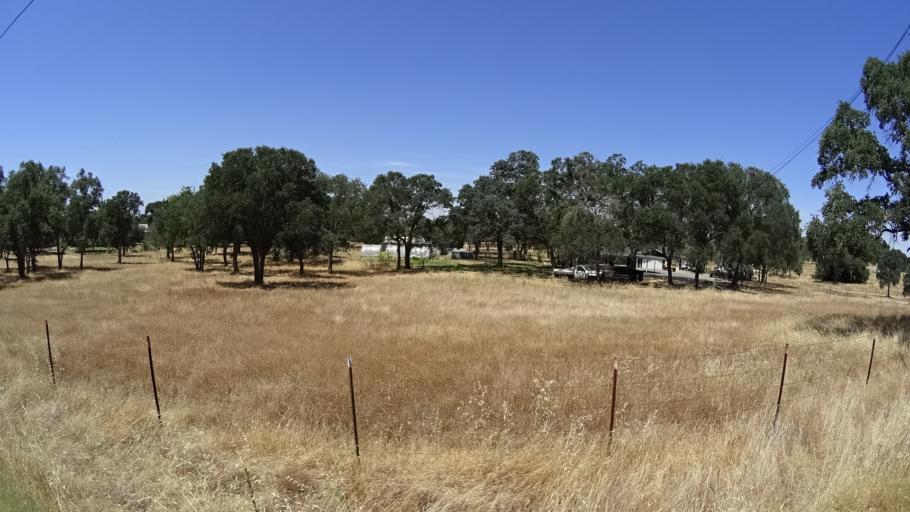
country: US
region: California
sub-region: Calaveras County
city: Rancho Calaveras
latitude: 38.1769
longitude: -120.9184
